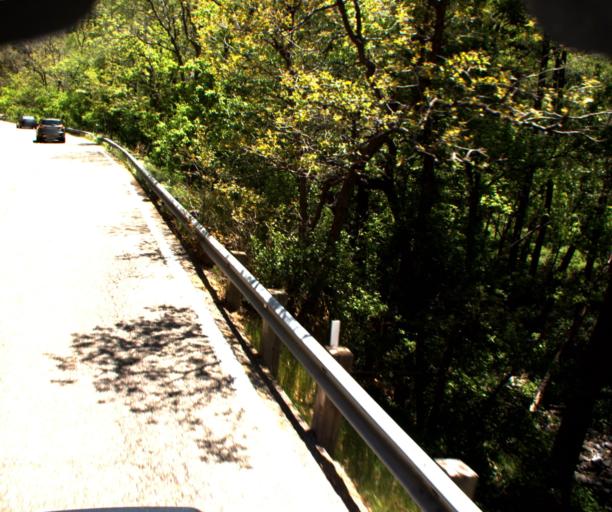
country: US
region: Arizona
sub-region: Coconino County
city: Kachina Village
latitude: 34.9936
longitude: -111.7369
